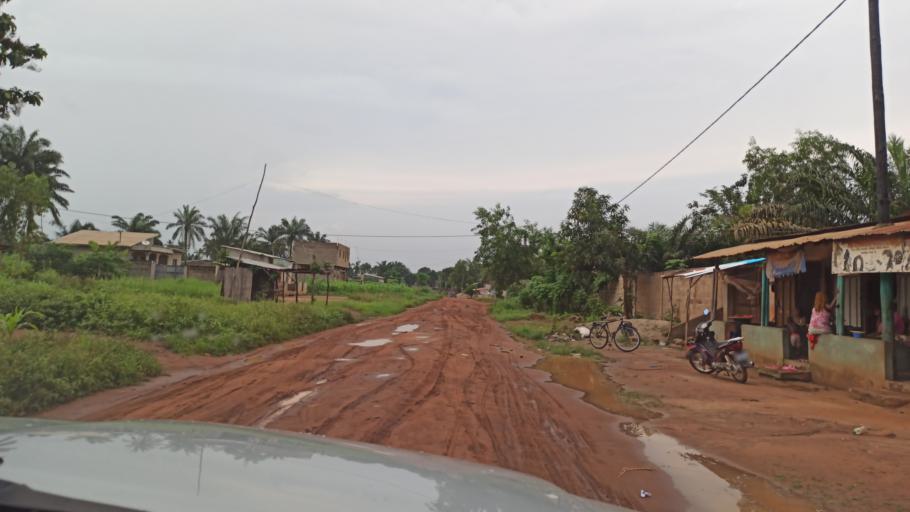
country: BJ
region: Queme
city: Porto-Novo
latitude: 6.4833
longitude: 2.6714
